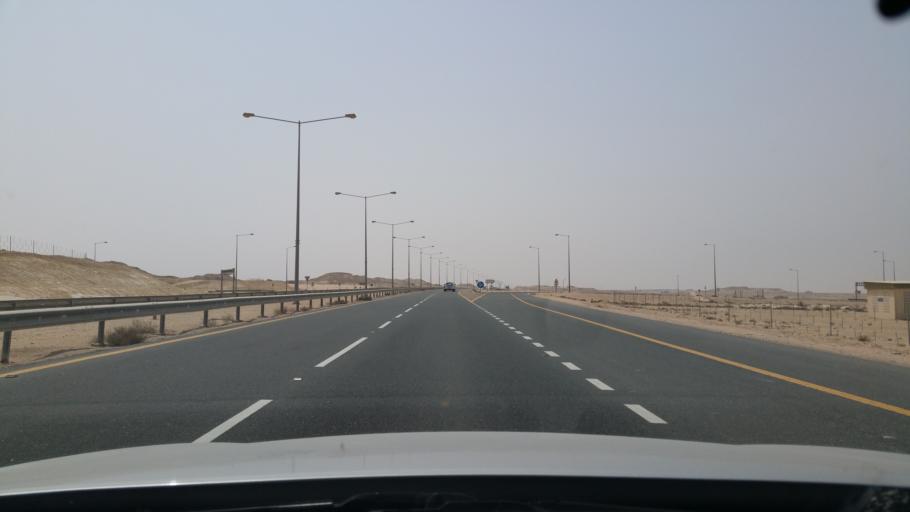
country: QA
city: Umm Bab
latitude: 25.2627
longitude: 50.7946
